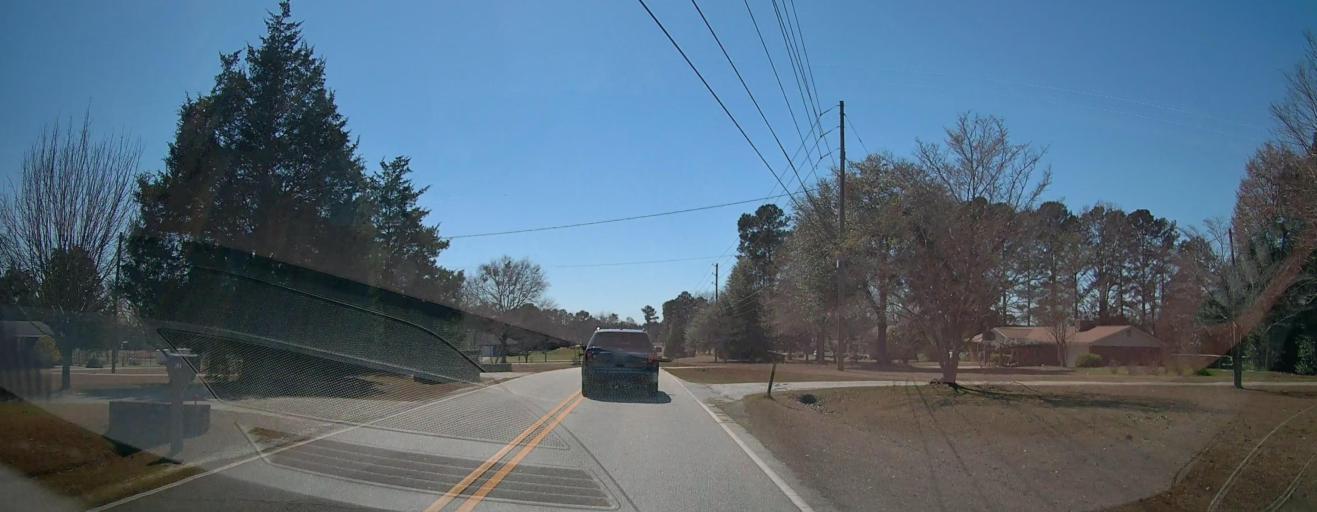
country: US
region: Georgia
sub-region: Houston County
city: Warner Robins
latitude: 32.5662
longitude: -83.6367
